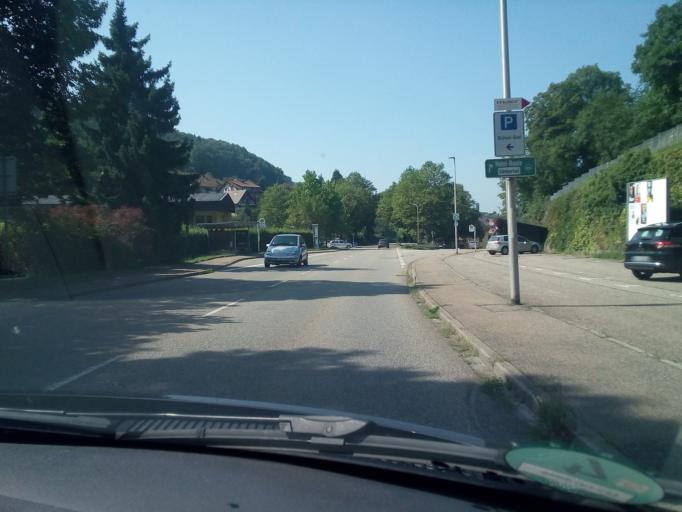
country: DE
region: Baden-Wuerttemberg
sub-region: Karlsruhe Region
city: Buhlertal
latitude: 48.6870
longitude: 8.1869
